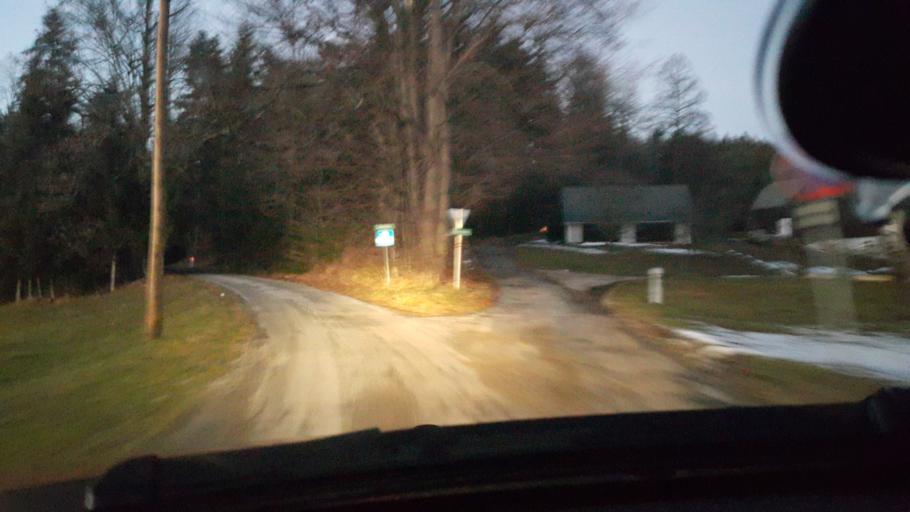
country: AT
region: Styria
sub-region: Politischer Bezirk Graz-Umgebung
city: Stiwoll
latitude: 47.1226
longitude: 15.2208
